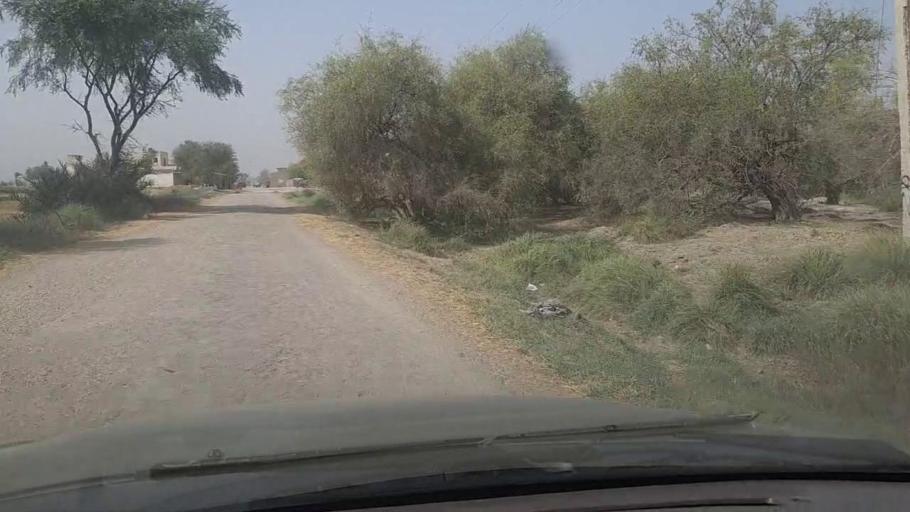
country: PK
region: Sindh
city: Garhi Yasin
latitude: 27.8712
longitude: 68.5584
